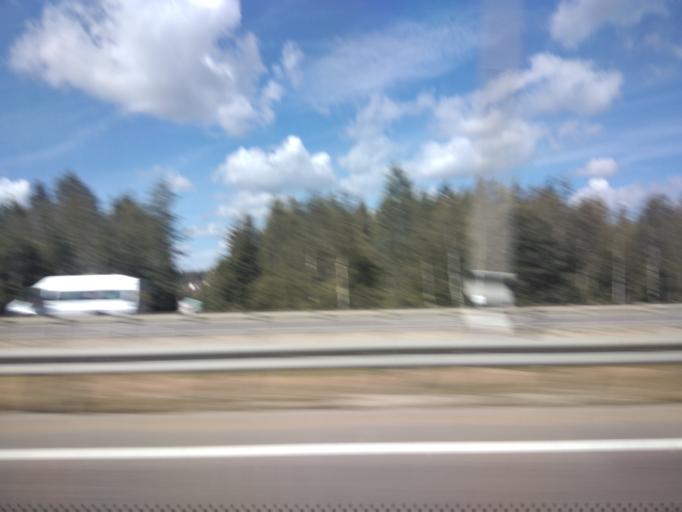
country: RU
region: Tula
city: Zaokskiy
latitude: 54.6364
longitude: 37.5005
